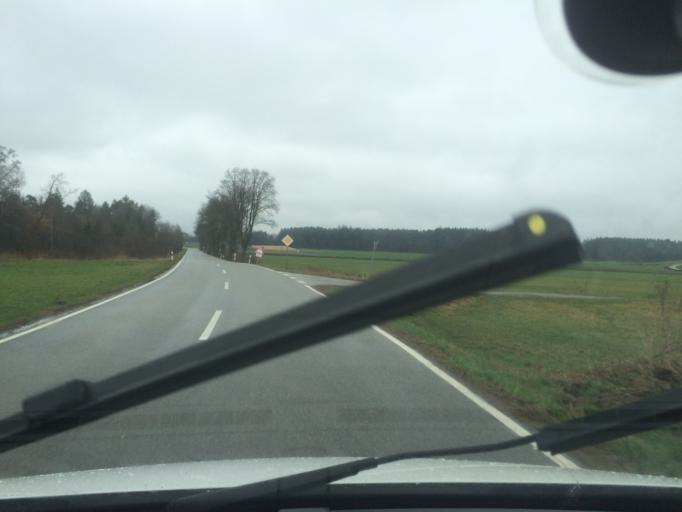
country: DE
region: Bavaria
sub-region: Upper Bavaria
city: Tuntenhausen
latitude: 47.9278
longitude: 12.0002
